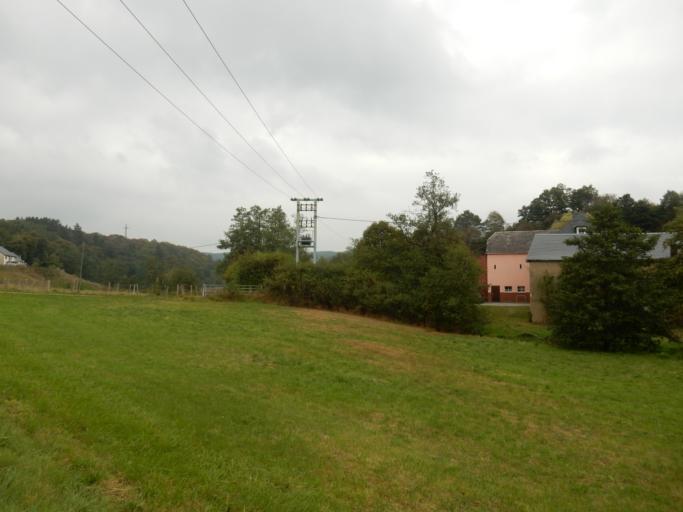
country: LU
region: Diekirch
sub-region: Canton de Wiltz
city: Winseler
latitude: 49.9632
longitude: 5.9039
